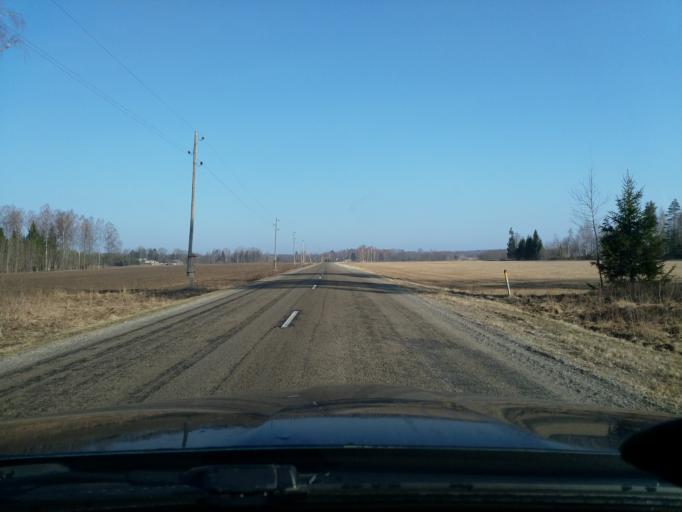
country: LV
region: Kuldigas Rajons
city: Kuldiga
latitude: 56.8742
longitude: 21.9386
